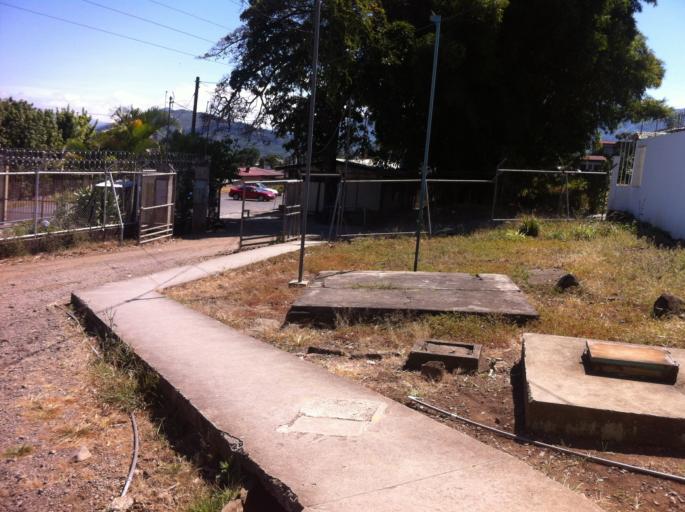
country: CR
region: San Jose
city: San Juan de Dios
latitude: 9.8778
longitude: -84.0857
